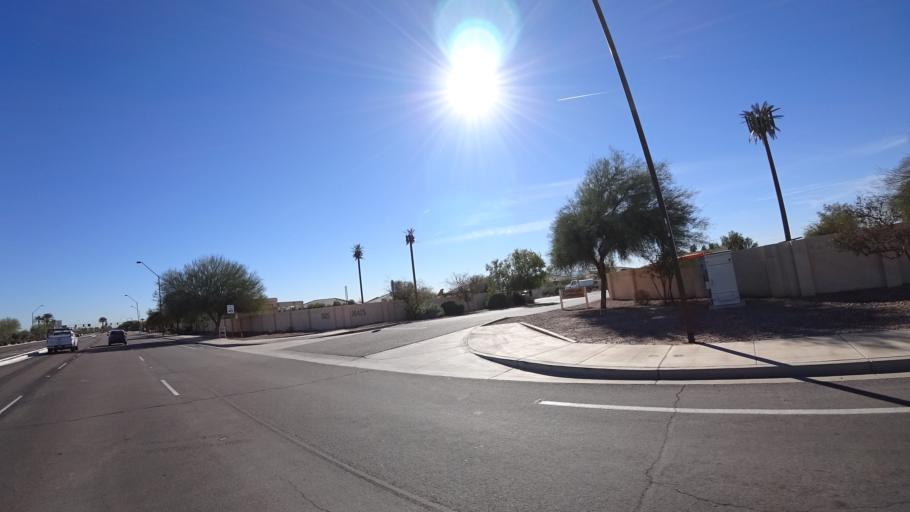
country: US
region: Arizona
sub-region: Maricopa County
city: Litchfield Park
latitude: 33.4937
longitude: -112.4129
